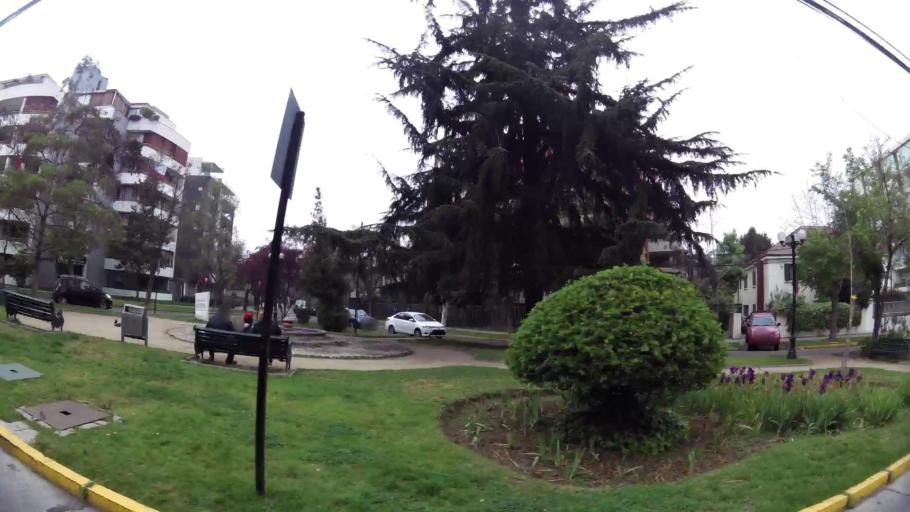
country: CL
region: Santiago Metropolitan
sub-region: Provincia de Santiago
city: Villa Presidente Frei, Nunoa, Santiago, Chile
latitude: -33.4287
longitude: -70.5932
